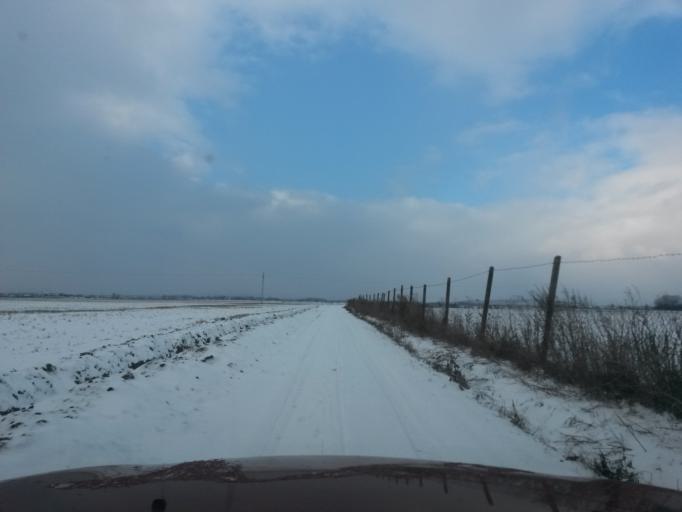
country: SK
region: Kosicky
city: Kosice
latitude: 48.6310
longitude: 21.3453
